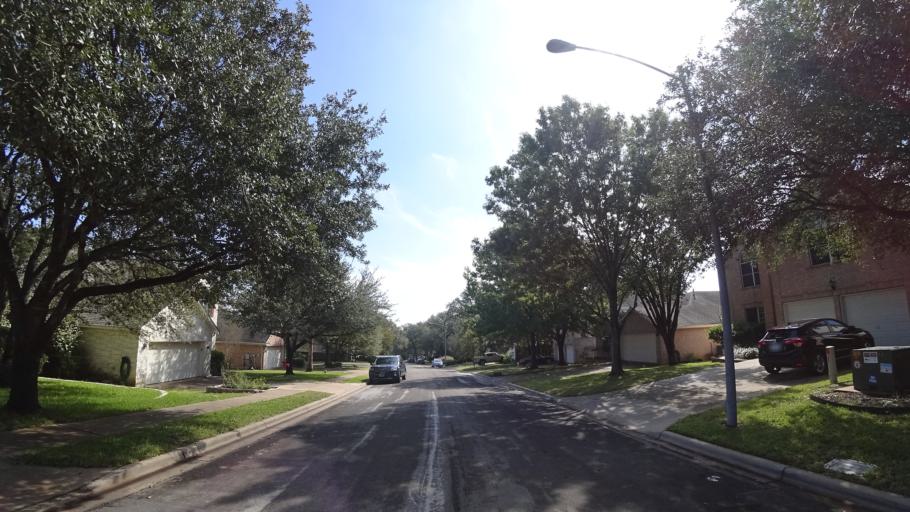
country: US
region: Texas
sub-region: Travis County
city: Shady Hollow
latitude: 30.2086
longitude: -97.8719
